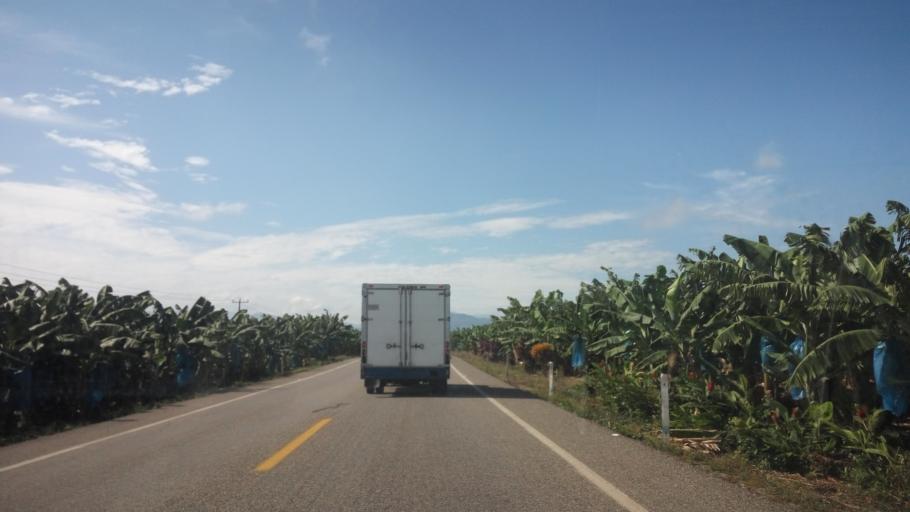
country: MX
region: Tabasco
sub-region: Teapa
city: Eureka y Belen
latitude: 17.6468
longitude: -92.9651
